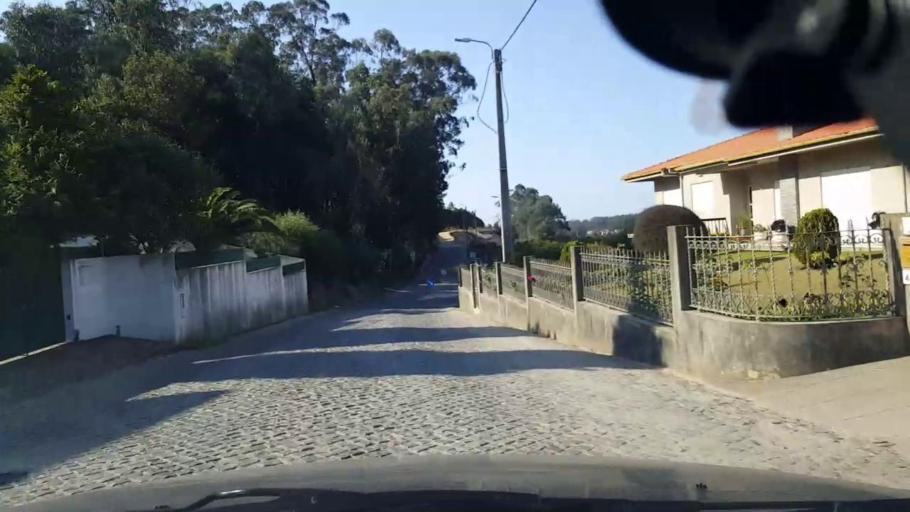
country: PT
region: Porto
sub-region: Vila do Conde
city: Arvore
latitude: 41.3529
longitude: -8.7185
